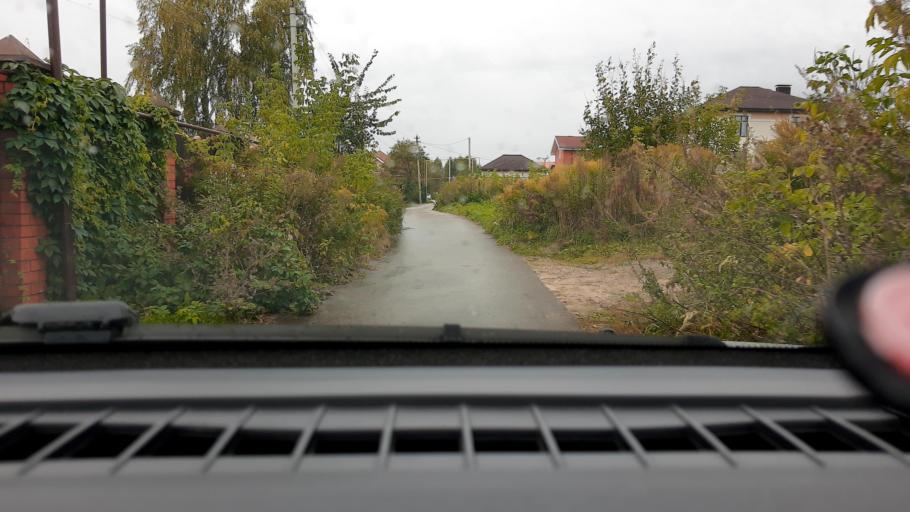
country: RU
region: Nizjnij Novgorod
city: Afonino
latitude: 56.1907
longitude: 44.0879
